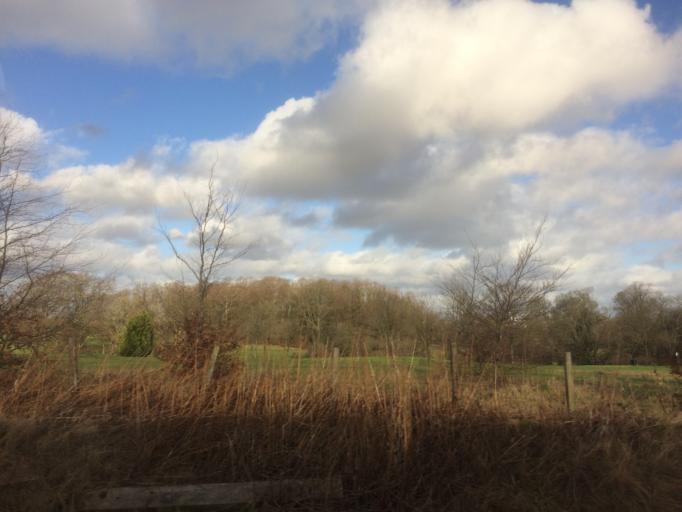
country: GB
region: Scotland
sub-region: East Renfrewshire
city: Newton Mearns
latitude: 55.7911
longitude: -4.3197
